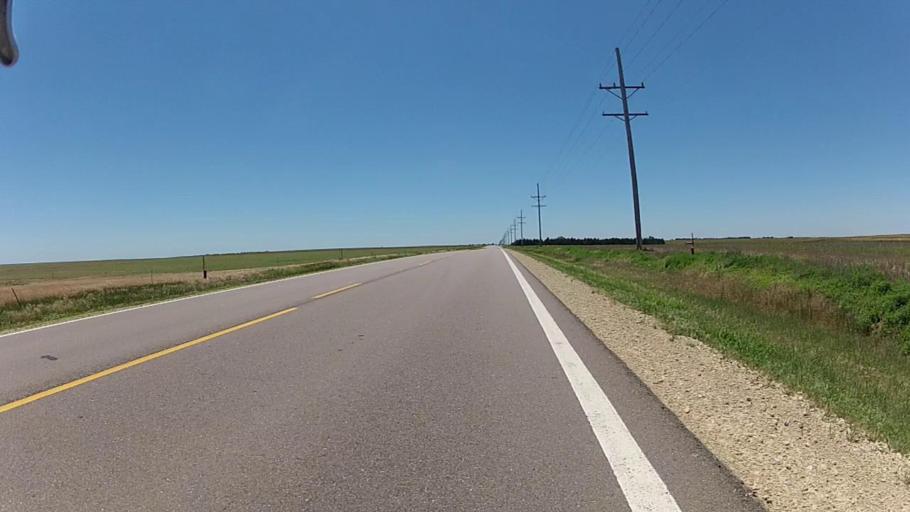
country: US
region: Kansas
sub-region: Kiowa County
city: Greensburg
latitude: 37.5377
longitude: -99.3209
